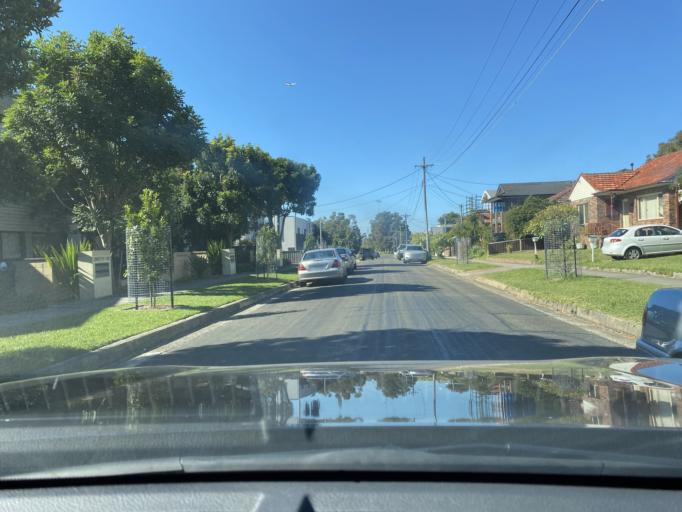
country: AU
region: New South Wales
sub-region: Canada Bay
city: Wareemba
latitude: -33.8539
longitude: 151.1343
